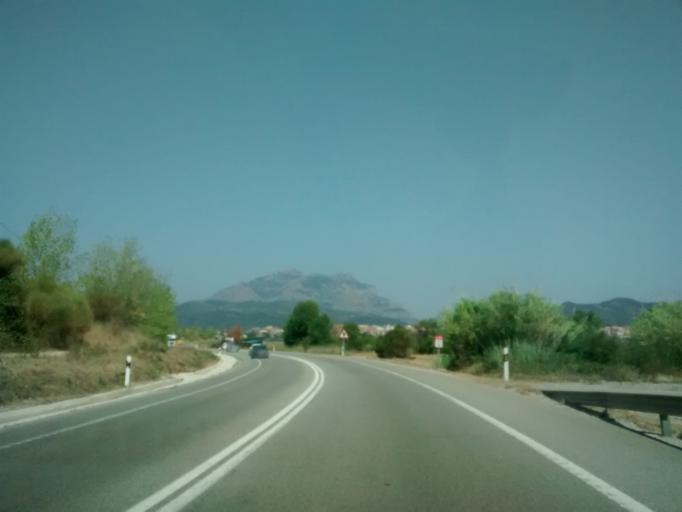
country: ES
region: Catalonia
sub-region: Provincia de Barcelona
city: Abrera
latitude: 41.5310
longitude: 1.9043
